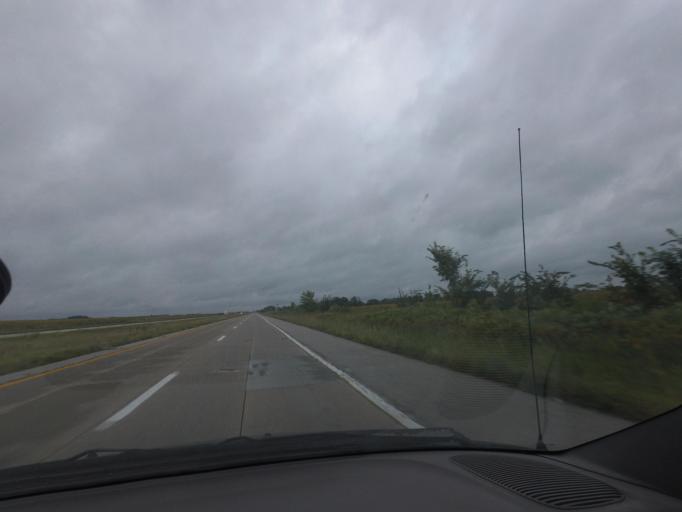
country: US
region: Missouri
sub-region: Marion County
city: Monroe City
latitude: 39.6642
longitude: -91.8449
